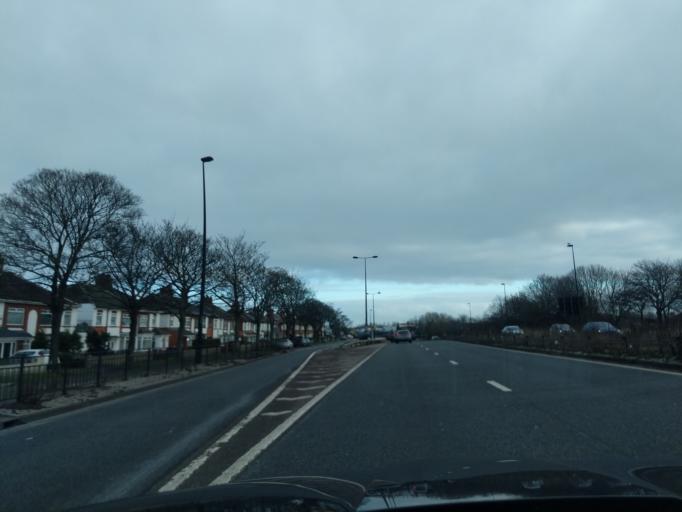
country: GB
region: England
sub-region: Borough of North Tyneside
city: Wallsend
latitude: 54.9940
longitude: -1.5716
